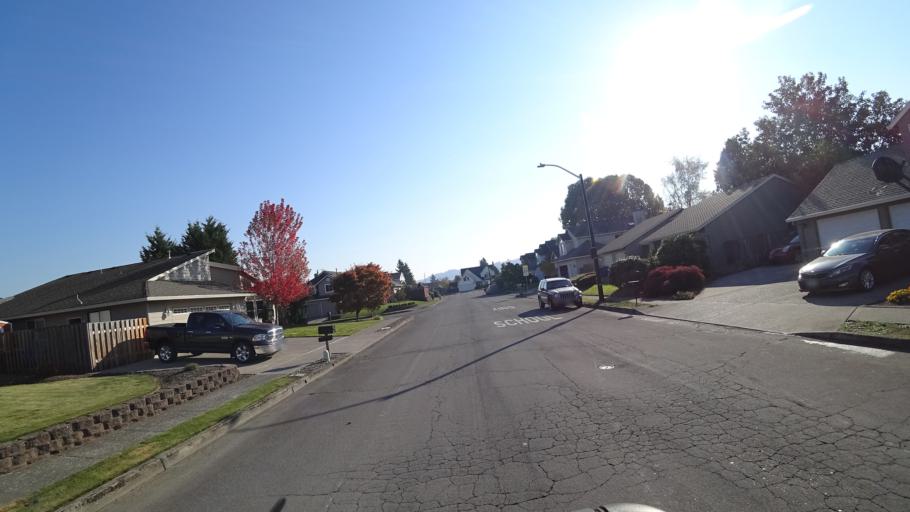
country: US
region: Oregon
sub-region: Multnomah County
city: Gresham
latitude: 45.5147
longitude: -122.4264
